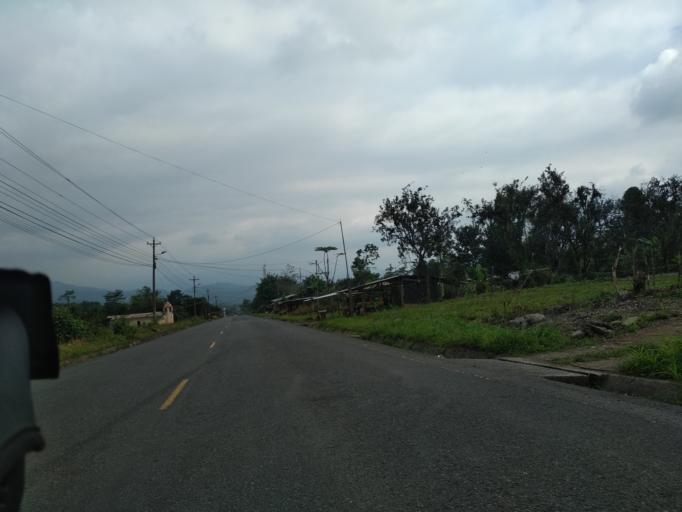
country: EC
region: Cotopaxi
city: La Mana
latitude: -0.8950
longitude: -79.1617
